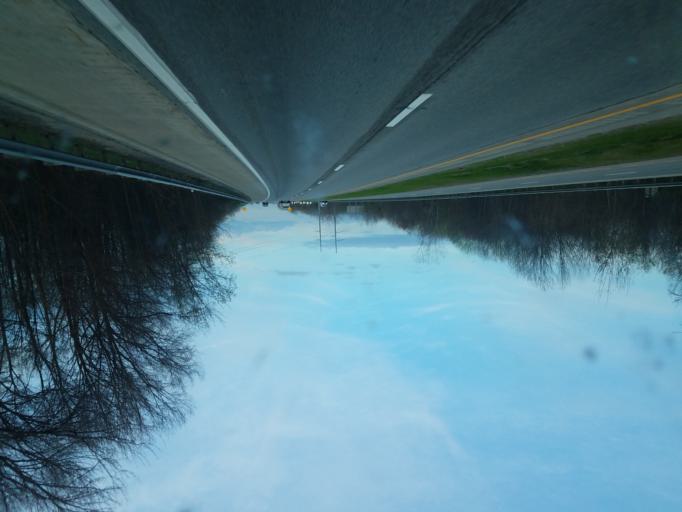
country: US
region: Ohio
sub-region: Lorain County
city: Lorain
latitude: 41.4099
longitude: -82.1566
